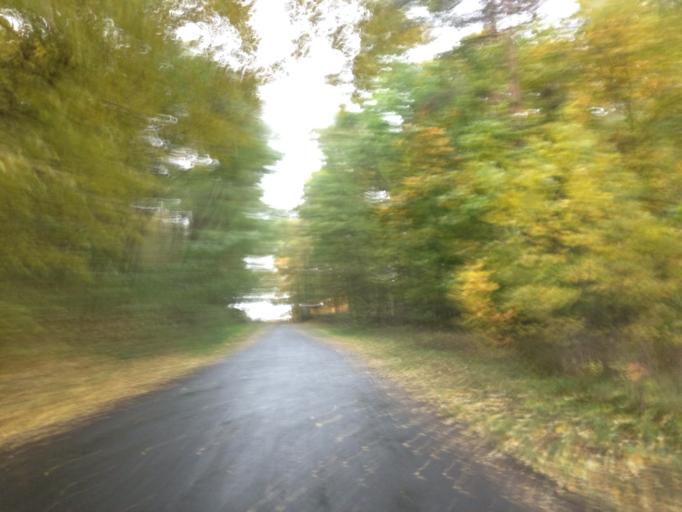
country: PL
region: Warmian-Masurian Voivodeship
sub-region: Powiat nowomiejski
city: Biskupiec
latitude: 53.5794
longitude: 19.4299
